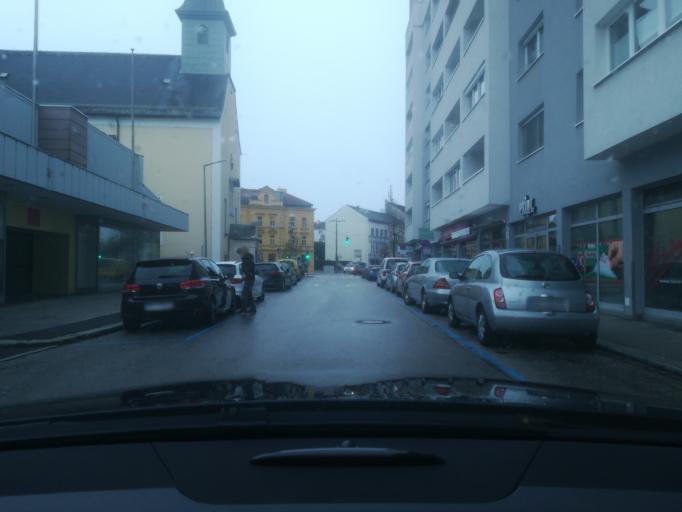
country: AT
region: Upper Austria
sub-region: Wels Stadt
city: Wels
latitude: 48.1599
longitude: 14.0286
